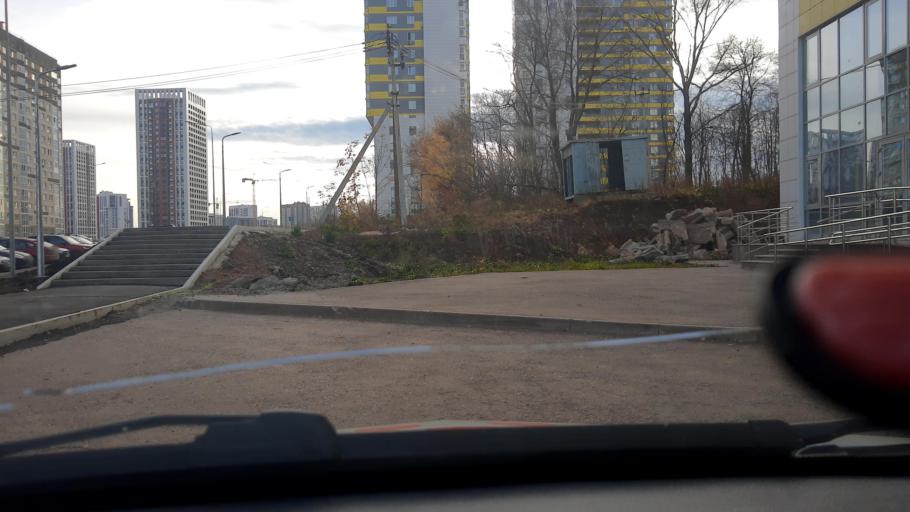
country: RU
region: Bashkortostan
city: Ufa
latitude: 54.7644
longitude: 56.0330
